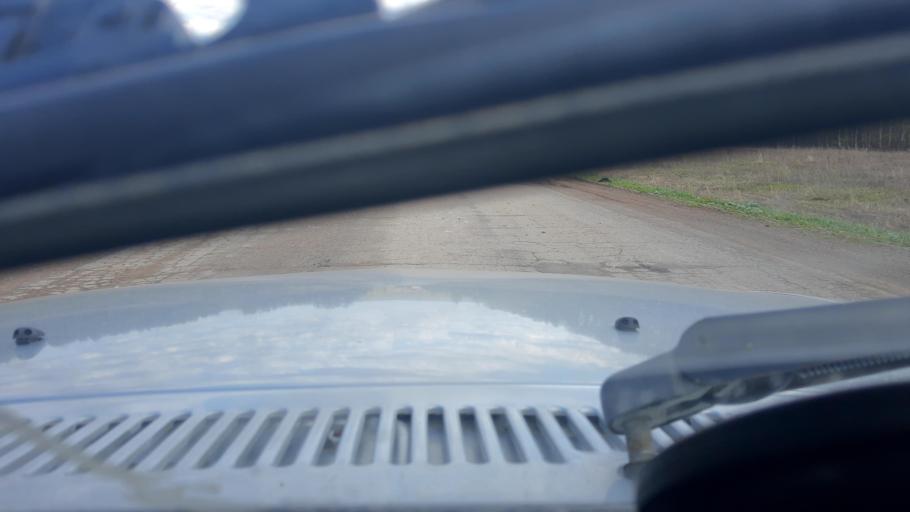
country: RU
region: Bashkortostan
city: Yazykovo
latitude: 55.2729
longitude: 56.2618
